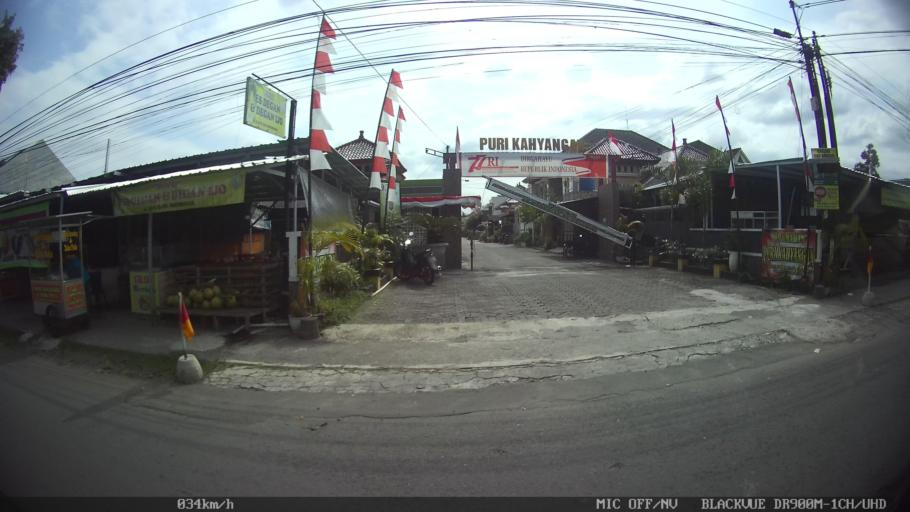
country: ID
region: Daerah Istimewa Yogyakarta
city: Depok
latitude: -7.7533
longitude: 110.4341
